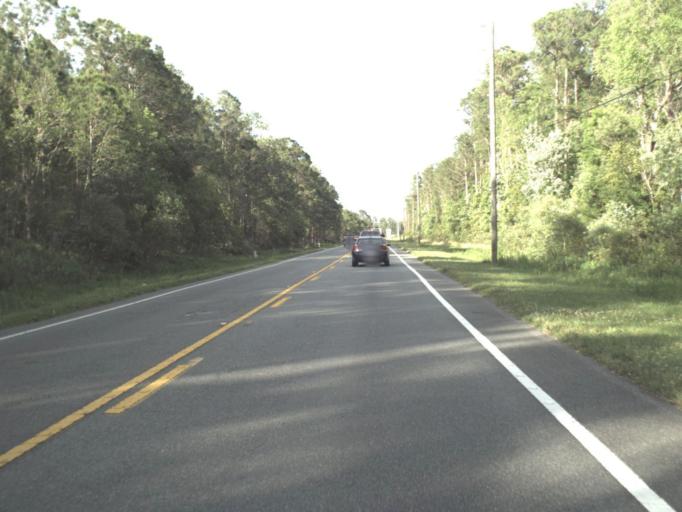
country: US
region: Florida
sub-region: Lake County
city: Astor
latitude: 29.1582
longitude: -81.5571
